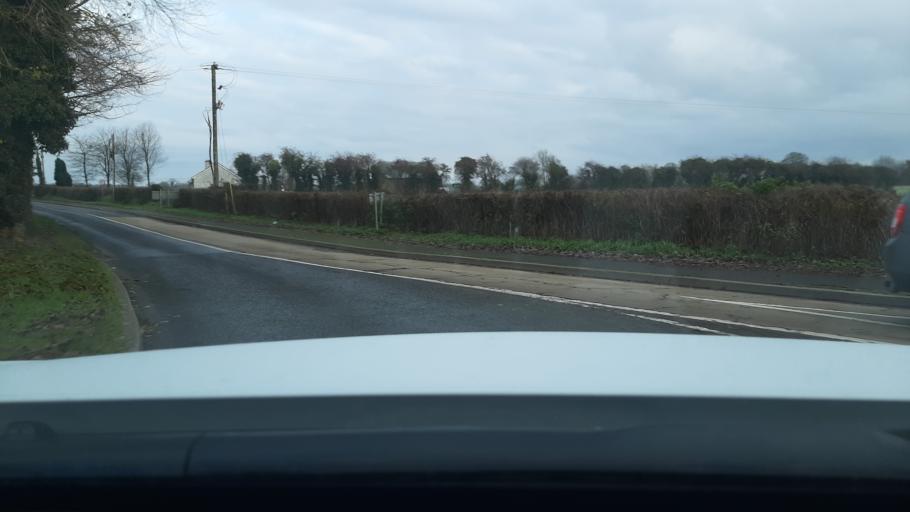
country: IE
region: Leinster
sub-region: Kildare
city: Rathangan
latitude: 53.2255
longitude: -7.0063
